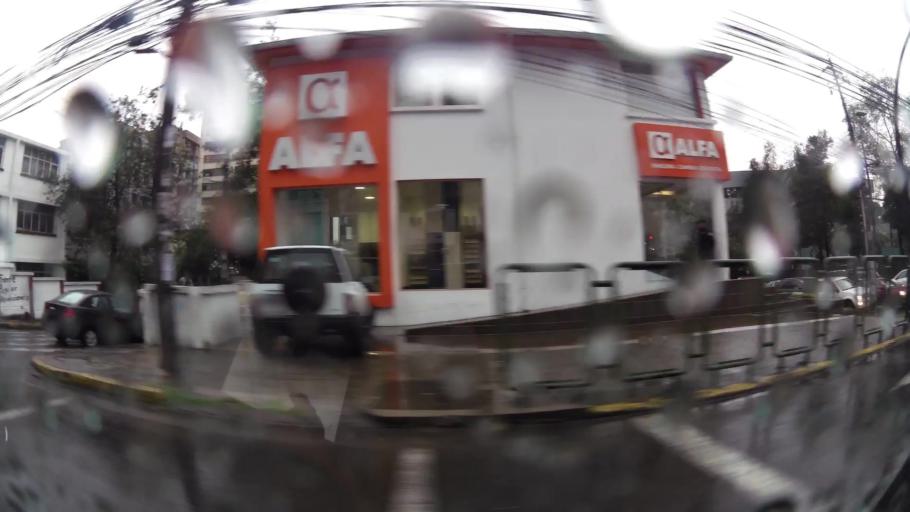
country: EC
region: Pichincha
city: Quito
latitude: -0.1944
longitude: -78.4822
